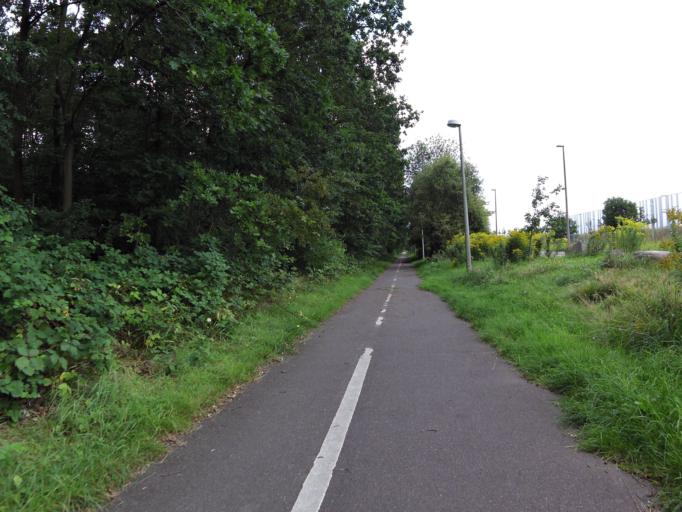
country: DE
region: Saxony
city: Rackwitz
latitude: 51.3873
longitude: 12.4083
